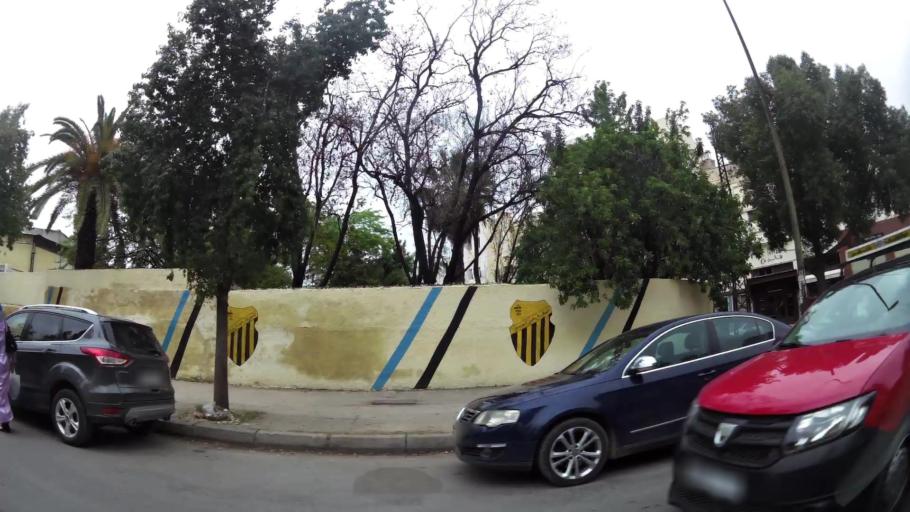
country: MA
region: Fes-Boulemane
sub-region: Fes
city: Fes
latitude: 34.0443
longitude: -5.0006
